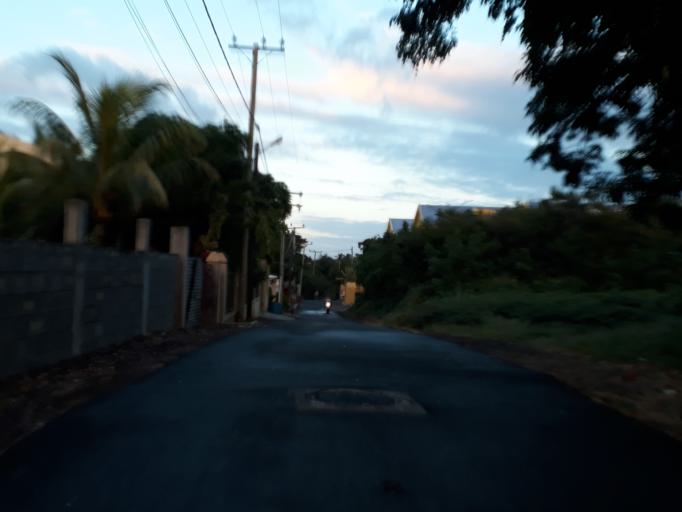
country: MU
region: Riviere du Rempart
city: Grand Baie
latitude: -20.0176
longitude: 57.5835
